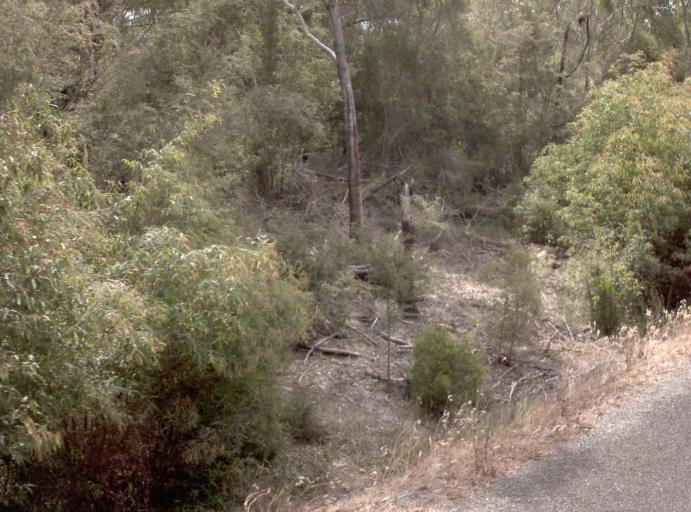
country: AU
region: New South Wales
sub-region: Bega Valley
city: Eden
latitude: -37.4680
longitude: 149.5883
